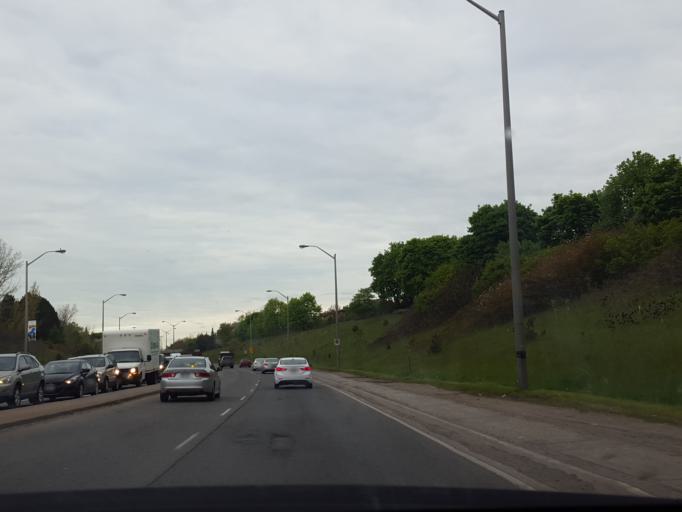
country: CA
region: Ontario
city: Toronto
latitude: 43.7053
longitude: -79.4944
